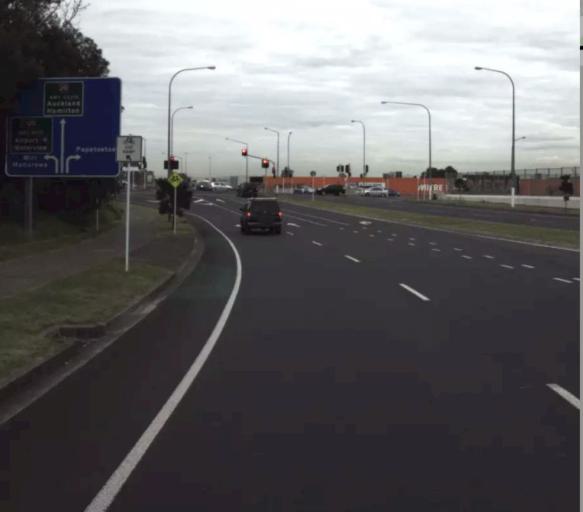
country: NZ
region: Auckland
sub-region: Auckland
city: Manukau City
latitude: -36.9950
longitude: 174.8757
